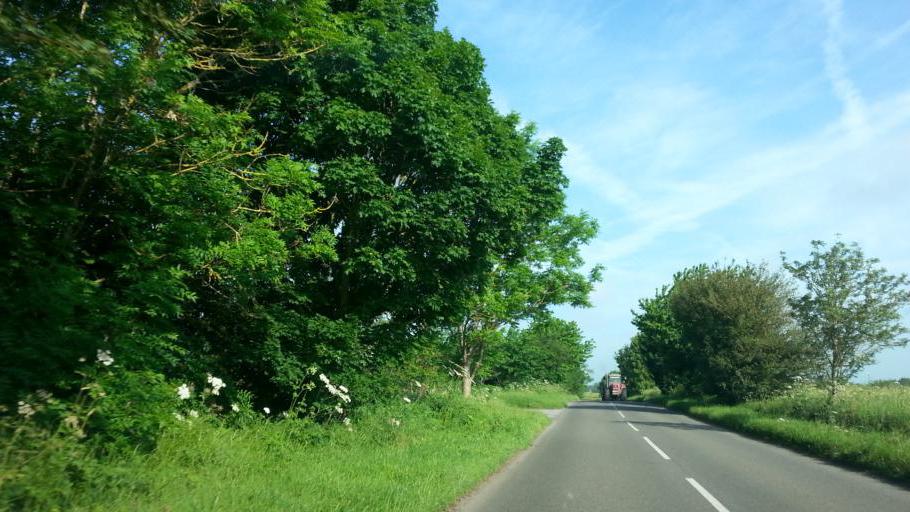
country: GB
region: England
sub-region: Nottinghamshire
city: Farndon
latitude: 53.0505
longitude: -0.8374
